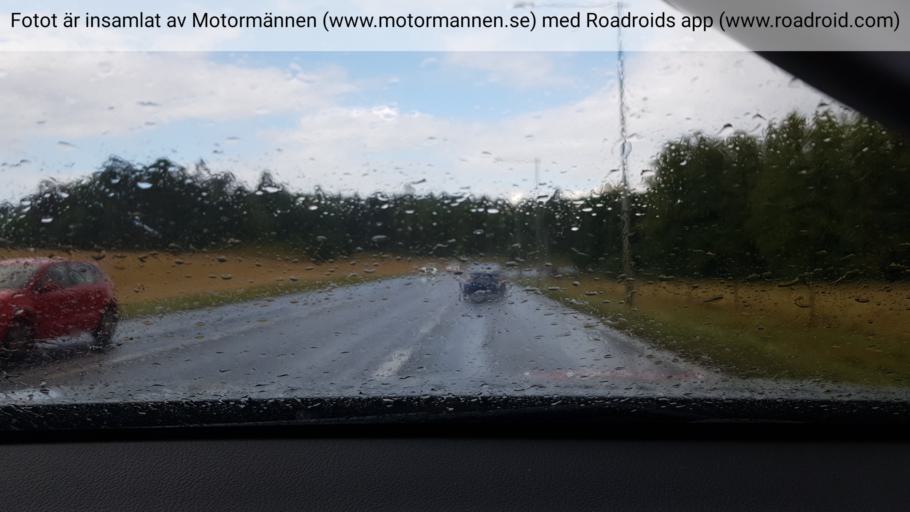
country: SE
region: Stockholm
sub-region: Ekero Kommun
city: Ekeroe
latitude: 59.3227
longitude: 17.8688
